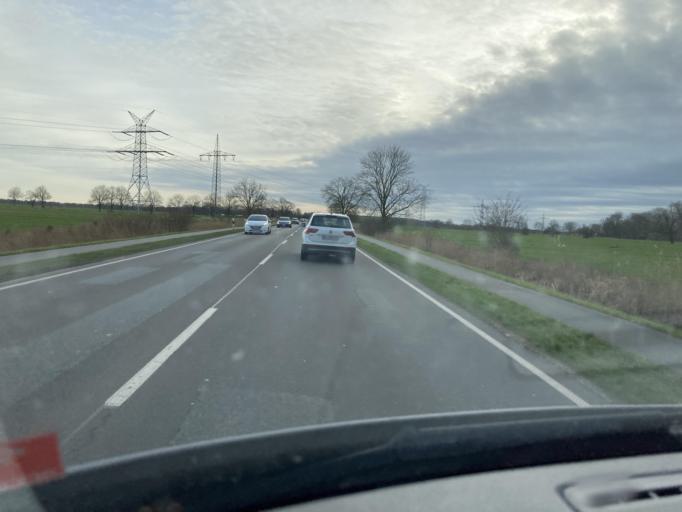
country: DE
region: Lower Saxony
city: Leer
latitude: 53.2143
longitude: 7.4841
